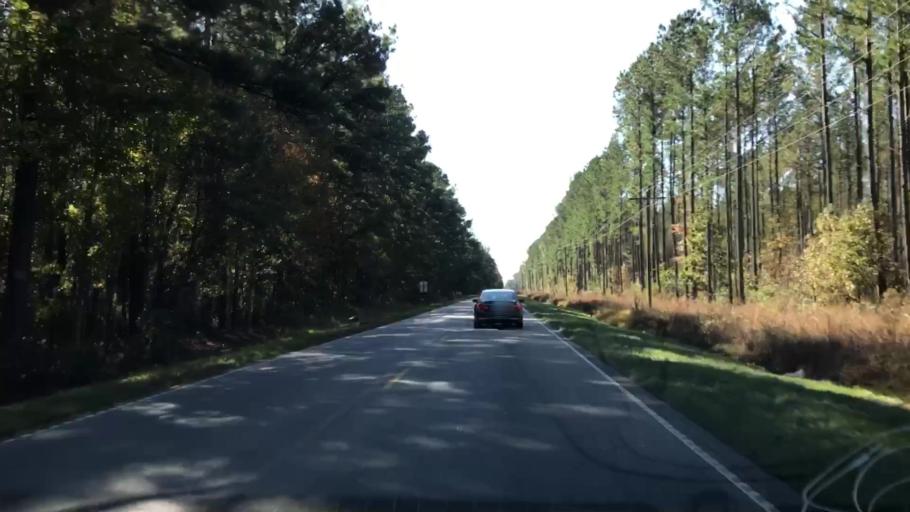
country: US
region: South Carolina
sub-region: Jasper County
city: Ridgeland
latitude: 32.3683
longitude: -80.9164
